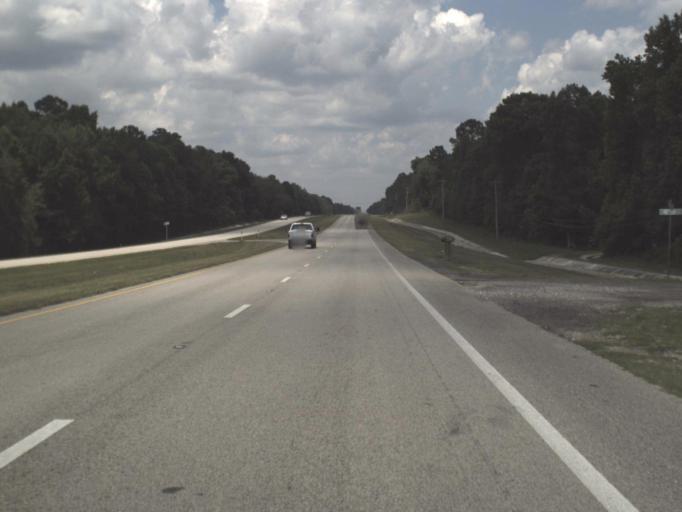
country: US
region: Florida
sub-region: Alachua County
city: Waldo
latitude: 29.7295
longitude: -82.2502
